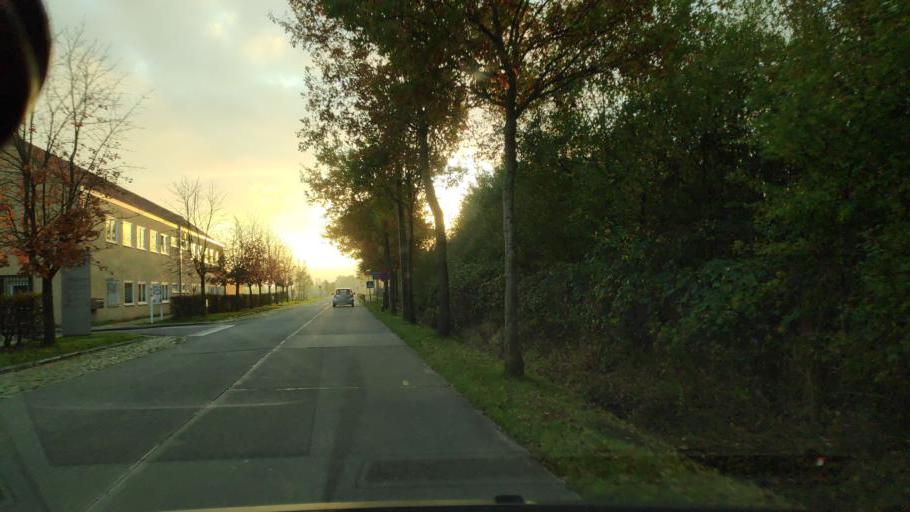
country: BE
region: Flanders
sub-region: Provincie West-Vlaanderen
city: Zedelgem
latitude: 51.1437
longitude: 3.1195
